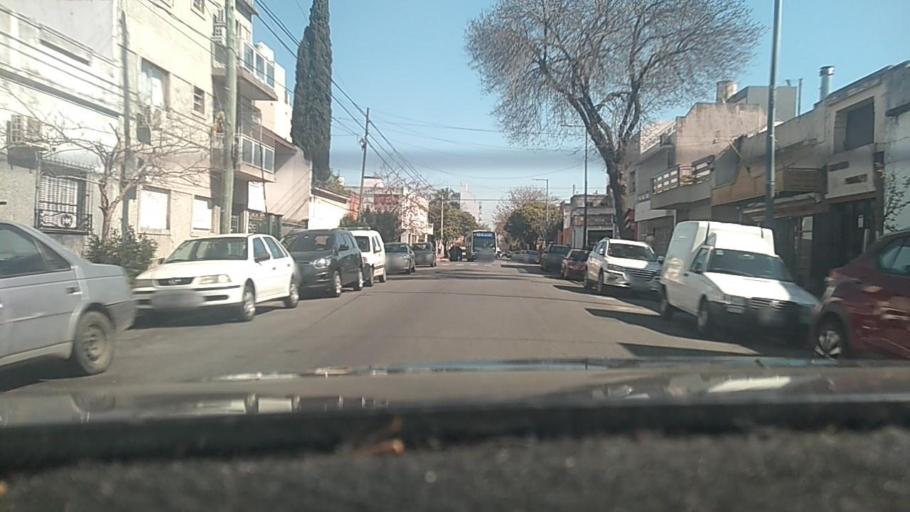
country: AR
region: Buenos Aires F.D.
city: Villa Santa Rita
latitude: -34.6091
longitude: -58.4979
